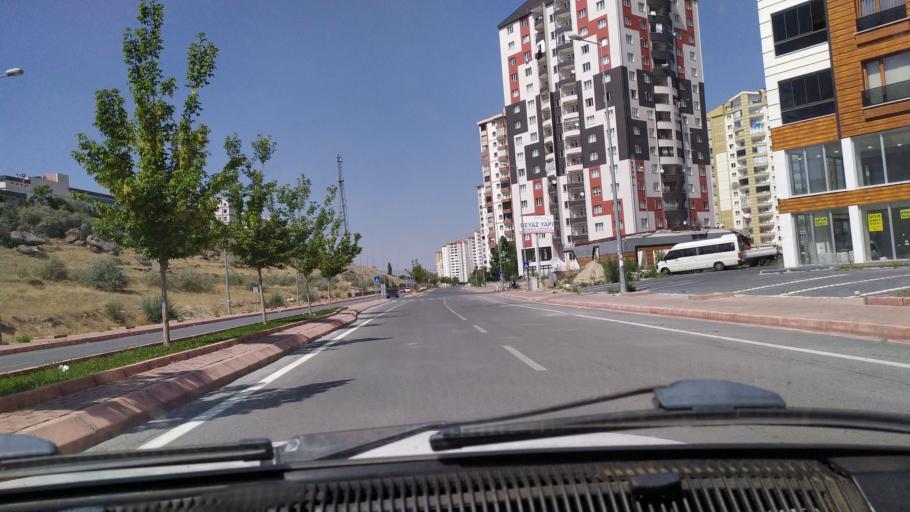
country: TR
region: Kayseri
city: Talas
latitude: 38.7105
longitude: 35.5567
